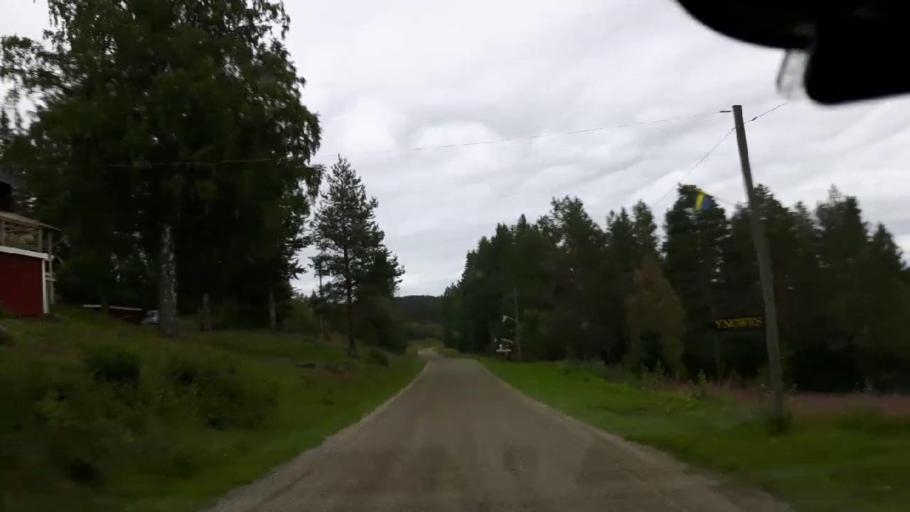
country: SE
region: Jaemtland
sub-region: Braecke Kommun
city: Braecke
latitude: 63.0136
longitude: 15.3780
